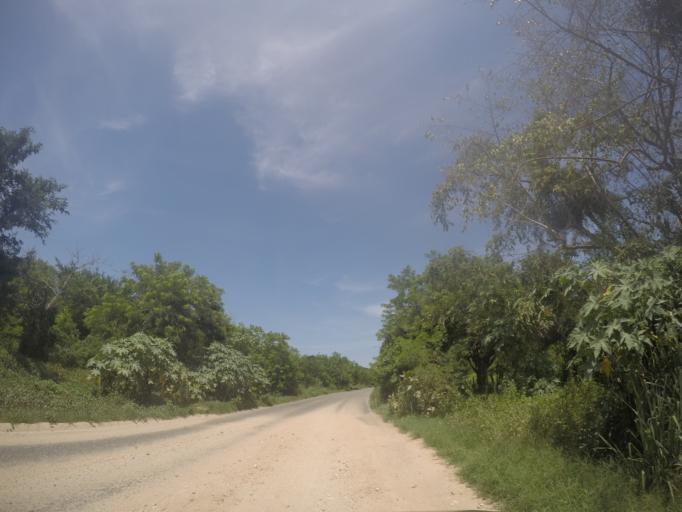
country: MX
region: Oaxaca
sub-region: Villa de Tututepec de Melchor Ocampo
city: Santa Rosa de Lima
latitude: 15.9925
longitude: -97.5381
